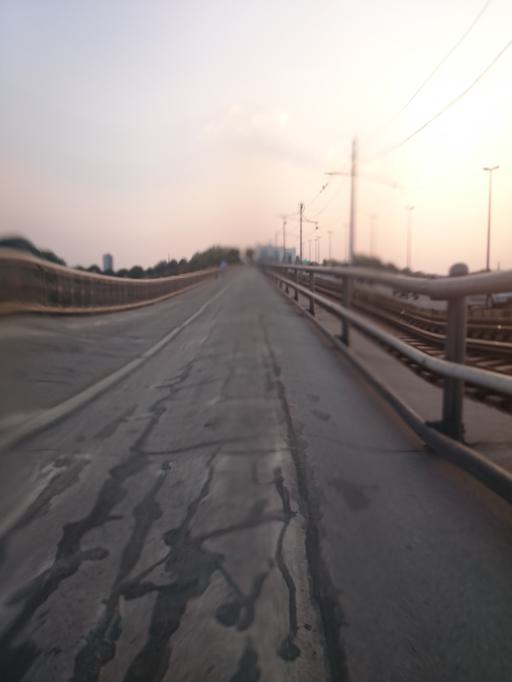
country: AT
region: Vienna
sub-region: Wien Stadt
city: Vienna
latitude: 48.2498
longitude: 16.3908
